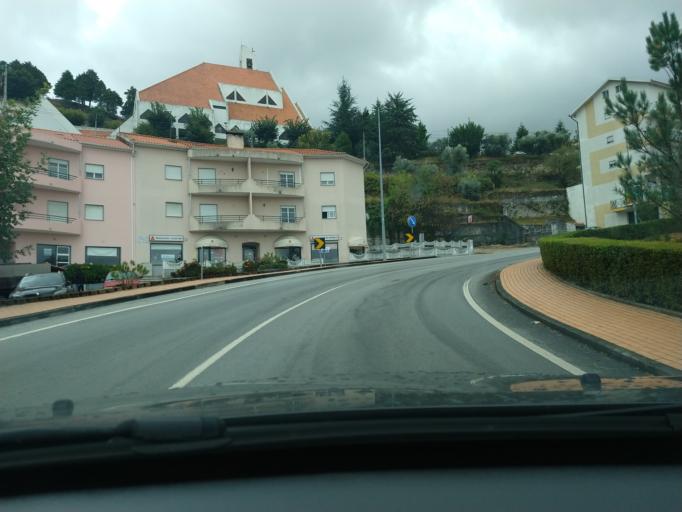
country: PT
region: Guarda
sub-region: Seia
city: Seia
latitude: 40.4028
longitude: -7.7113
